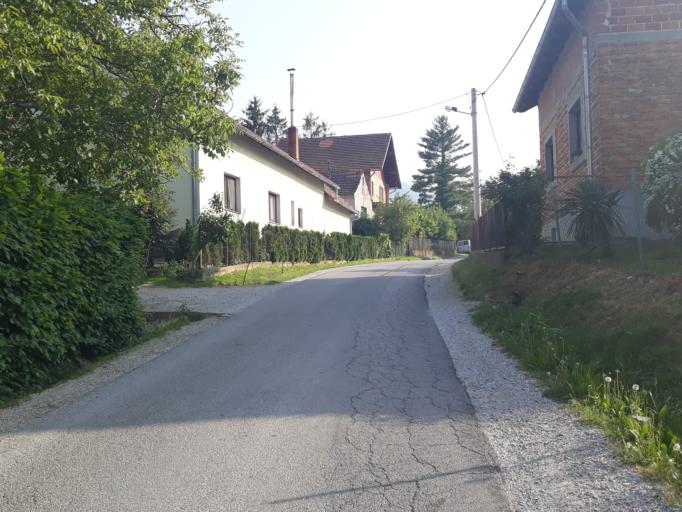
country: HR
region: Varazdinska
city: Ivanec
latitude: 46.2232
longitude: 16.1463
